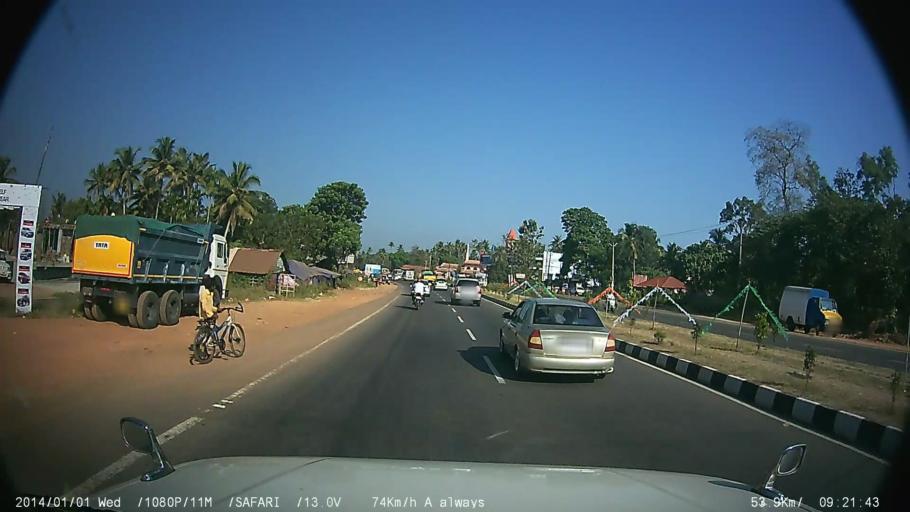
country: IN
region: Kerala
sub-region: Thrissur District
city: Kizhake Chalakudi
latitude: 10.2720
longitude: 76.3475
